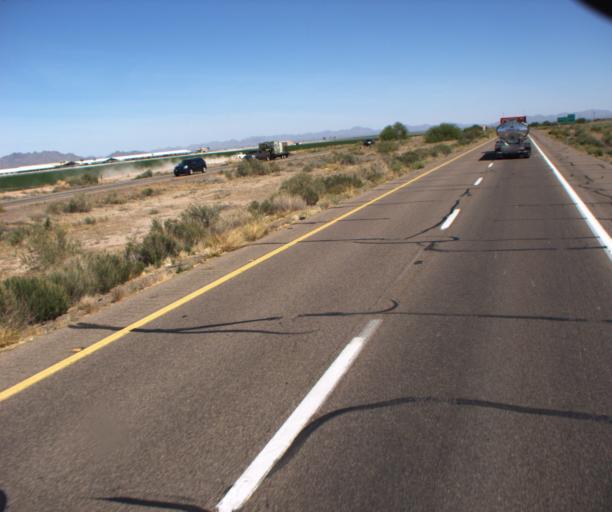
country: US
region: Arizona
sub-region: Maricopa County
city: Gila Bend
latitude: 32.9301
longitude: -112.8197
